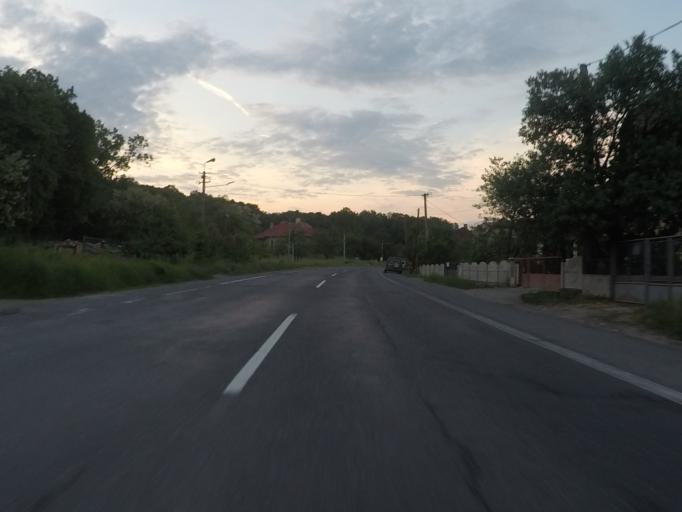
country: SK
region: Banskobystricky
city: Rimavska Sobota
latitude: 48.4704
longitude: 19.9501
